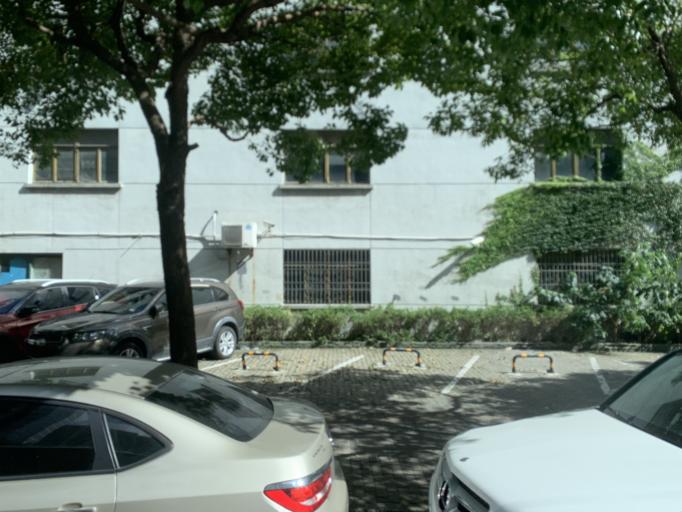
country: CN
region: Shanghai Shi
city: Pudong
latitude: 31.2408
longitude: 121.5355
